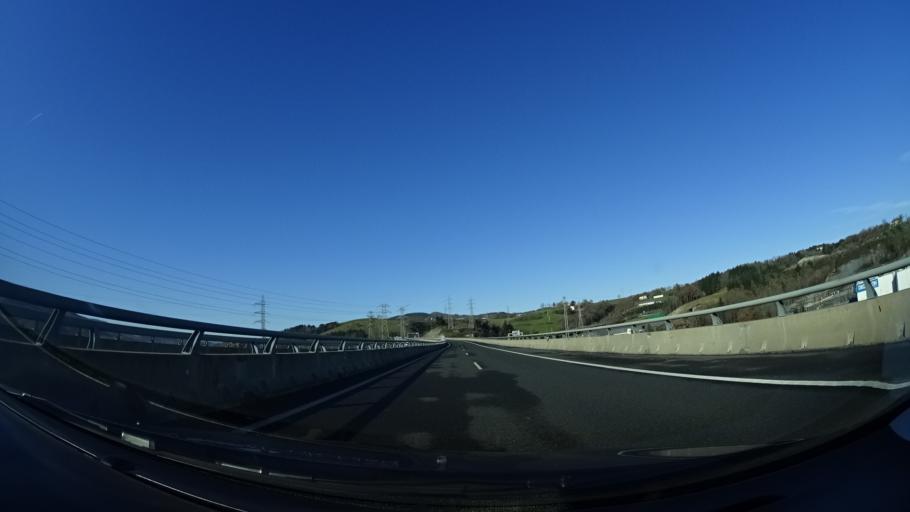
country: ES
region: Basque Country
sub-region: Provincia de Guipuzcoa
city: Lasarte
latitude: 43.2772
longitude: -2.0136
